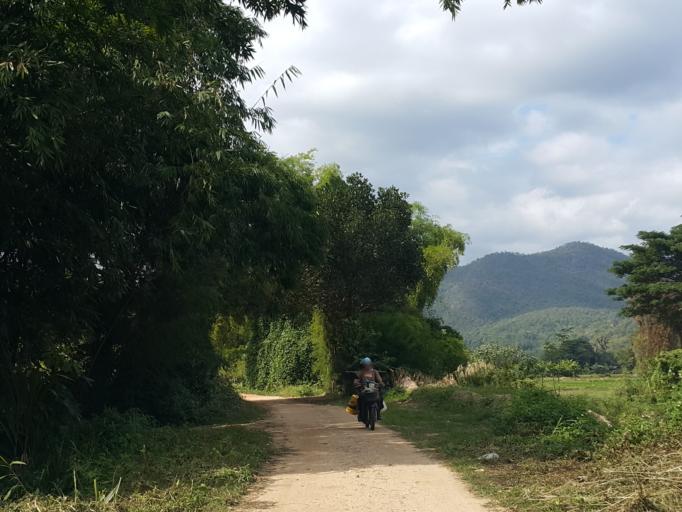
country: TH
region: Lampang
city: Chae Hom
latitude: 18.5637
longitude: 99.4537
